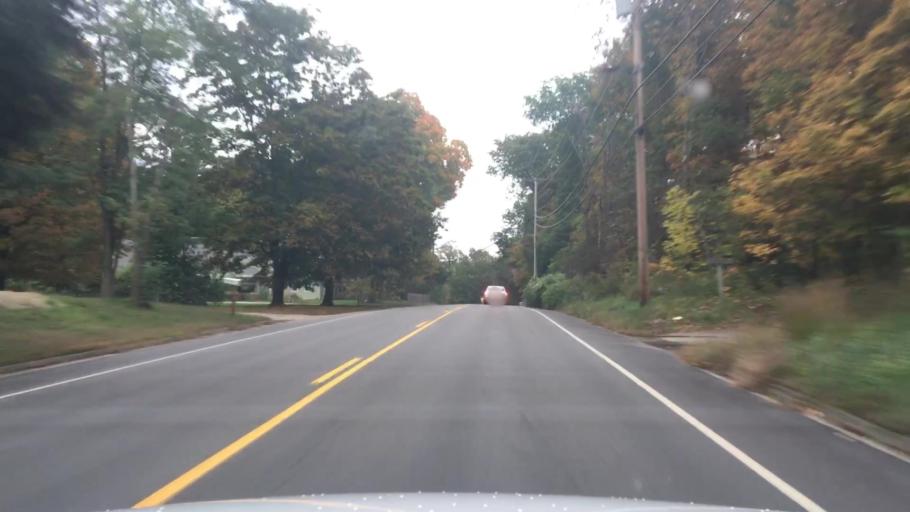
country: US
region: Maine
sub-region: York County
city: Hollis Center
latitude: 43.6109
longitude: -70.5571
